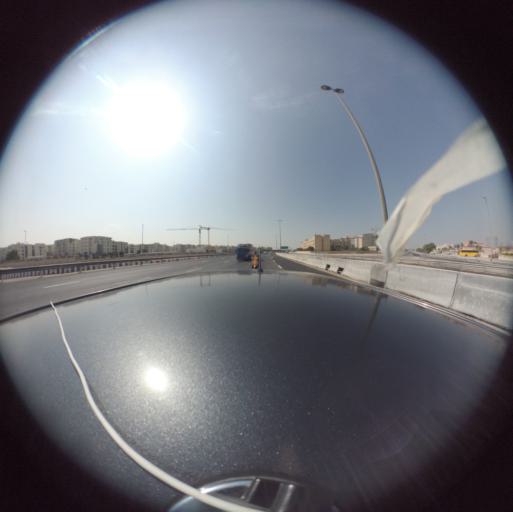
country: AE
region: Dubai
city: Dubai
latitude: 25.1444
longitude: 55.2590
